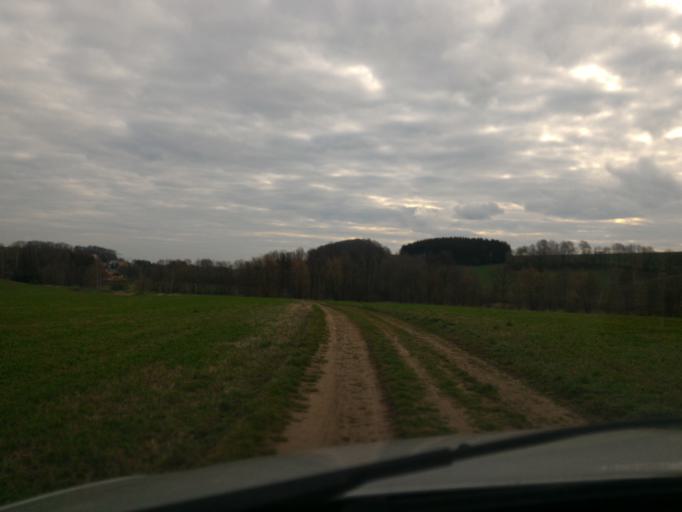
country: DE
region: Saxony
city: Eibau
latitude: 50.9699
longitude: 14.6702
